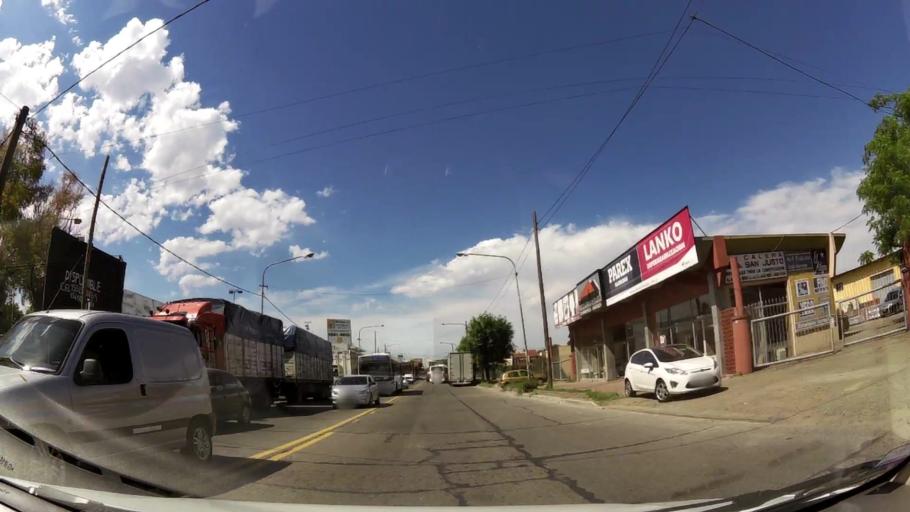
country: AR
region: Buenos Aires
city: San Justo
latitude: -34.6708
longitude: -58.5587
